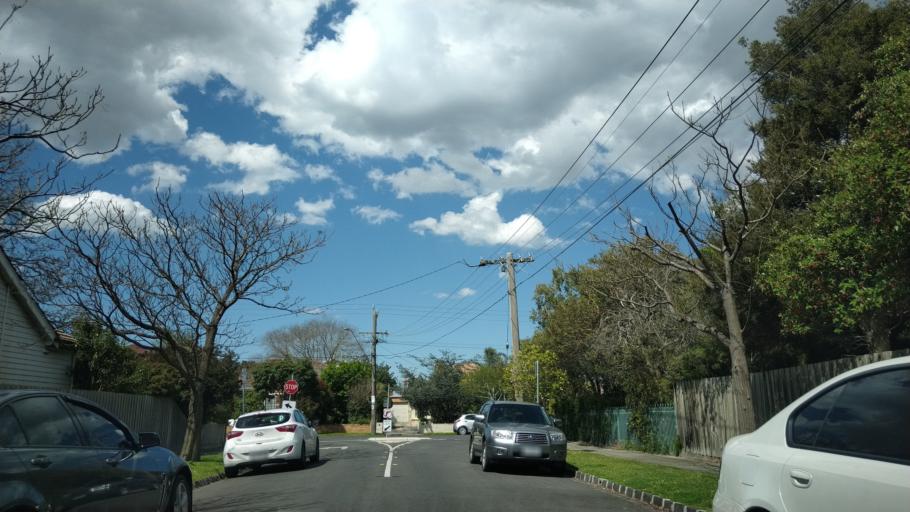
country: AU
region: Victoria
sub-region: Glen Eira
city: Carnegie
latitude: -37.8923
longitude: 145.0560
